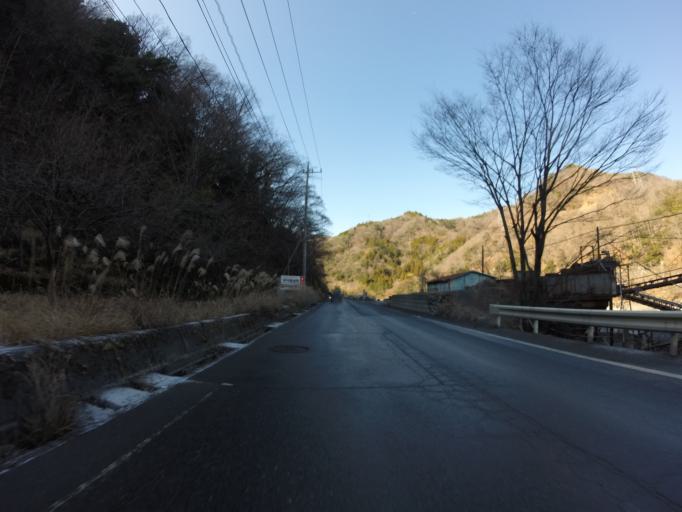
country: JP
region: Yamanashi
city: Ryuo
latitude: 35.4222
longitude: 138.4031
